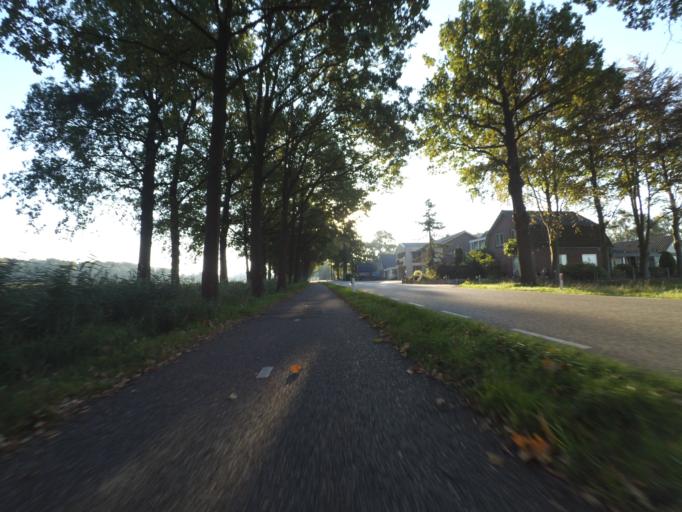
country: NL
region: Utrecht
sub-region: Gemeente Leusden
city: Leusden
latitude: 52.1499
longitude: 5.4428
